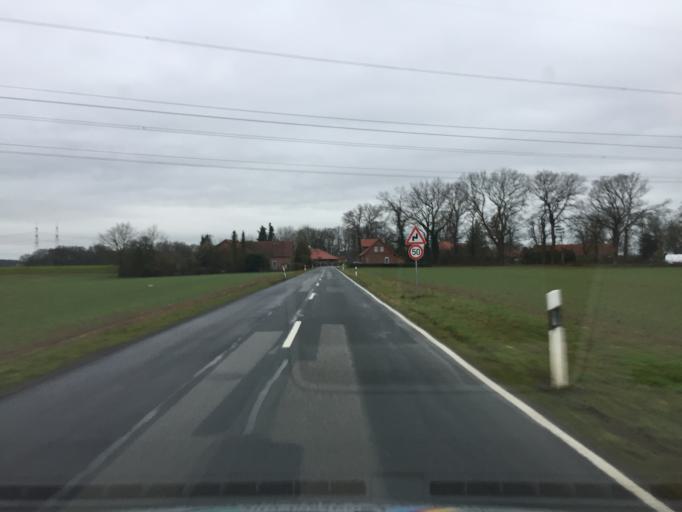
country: DE
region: Lower Saxony
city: Steyerberg
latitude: 52.5556
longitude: 9.0270
